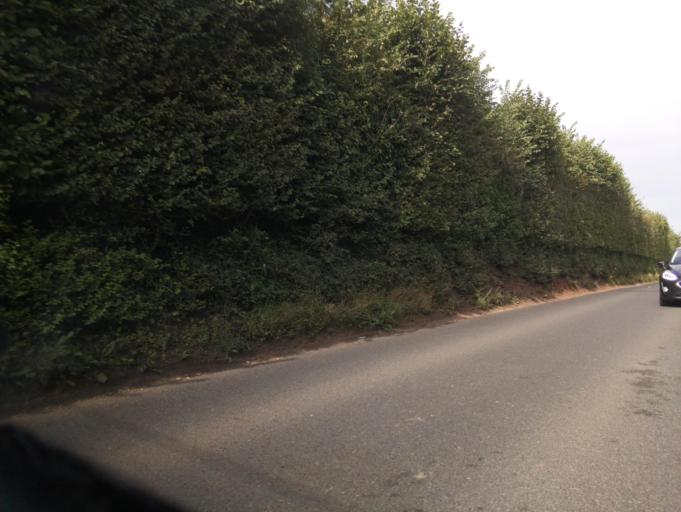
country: GB
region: England
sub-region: North Somerset
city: Winford
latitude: 51.3801
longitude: -2.6581
